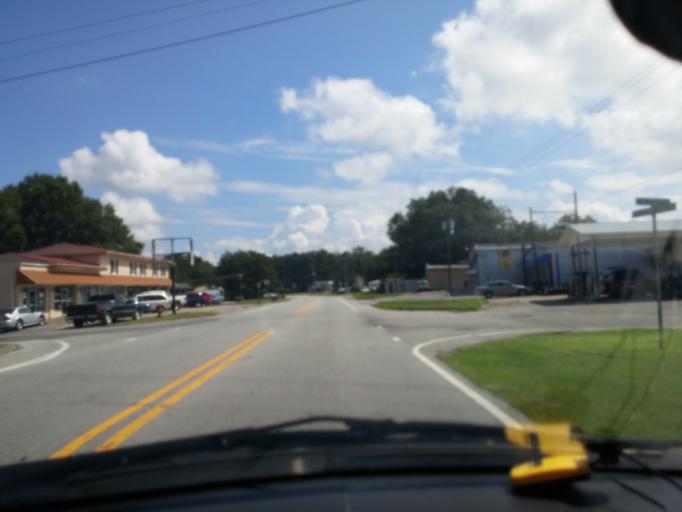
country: US
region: North Carolina
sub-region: Duplin County
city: Beulaville
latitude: 35.0566
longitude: -77.7466
